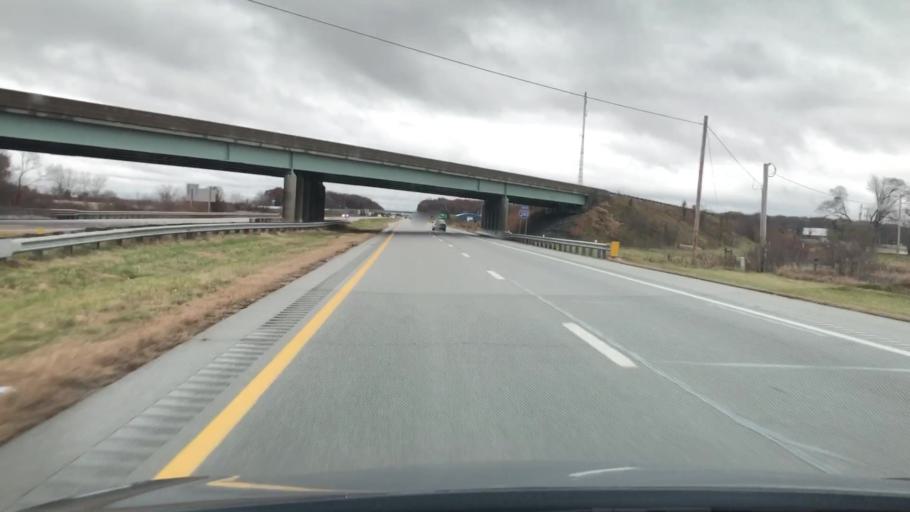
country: US
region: Ohio
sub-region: Wood County
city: Walbridge
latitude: 41.5791
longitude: -83.4740
